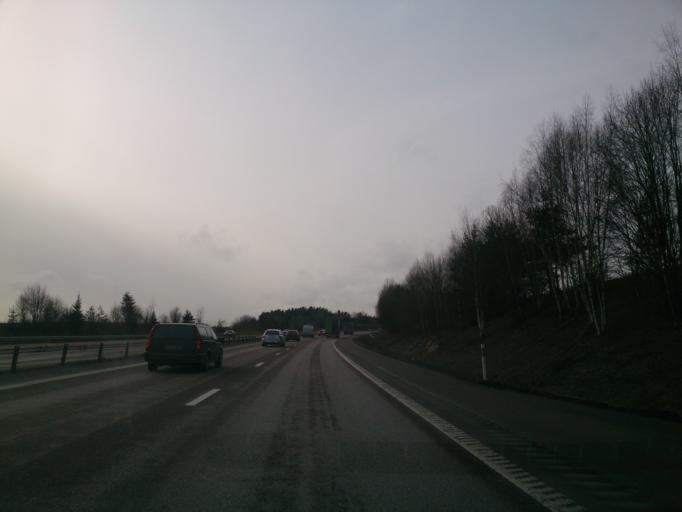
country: SE
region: Soedermanland
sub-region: Gnesta Kommun
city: Gnesta
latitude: 58.8795
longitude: 17.2413
